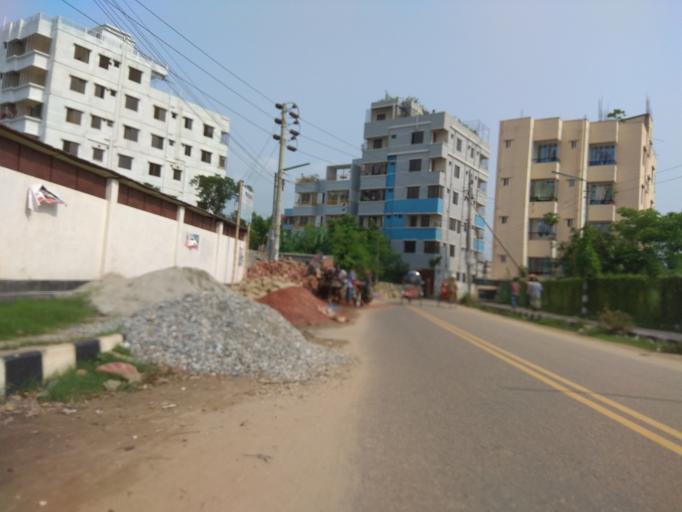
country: BD
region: Dhaka
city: Tungi
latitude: 23.8308
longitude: 90.3555
